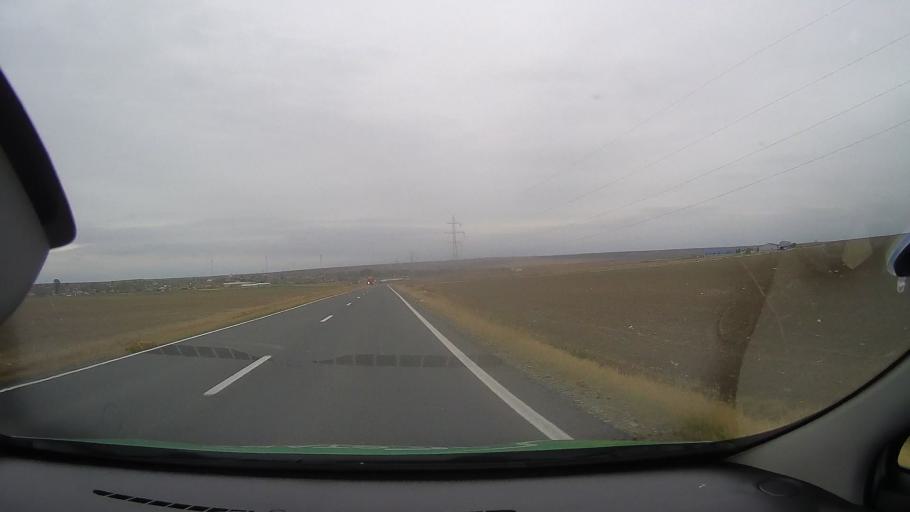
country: RO
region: Constanta
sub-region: Comuna Nicolae Balcescu
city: Dorobantu
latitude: 44.4177
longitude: 28.3144
